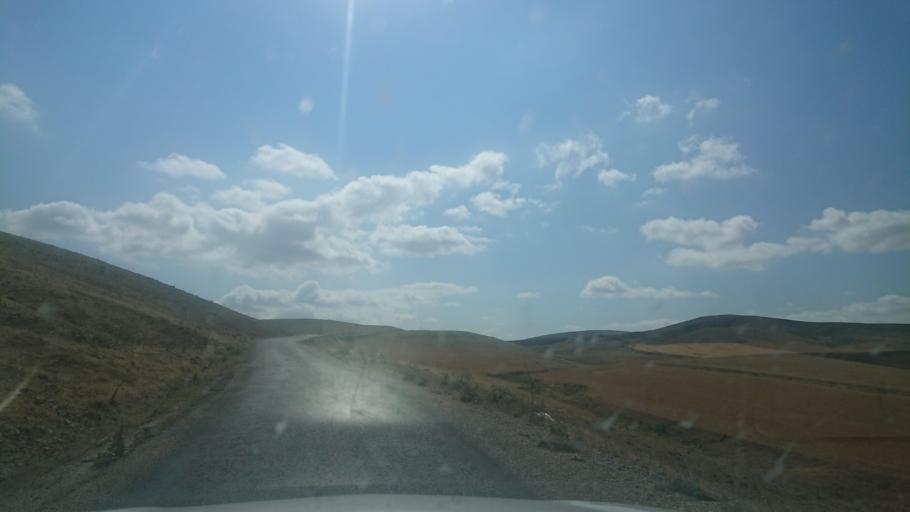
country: TR
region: Aksaray
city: Sariyahsi
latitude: 39.0067
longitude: 33.9529
